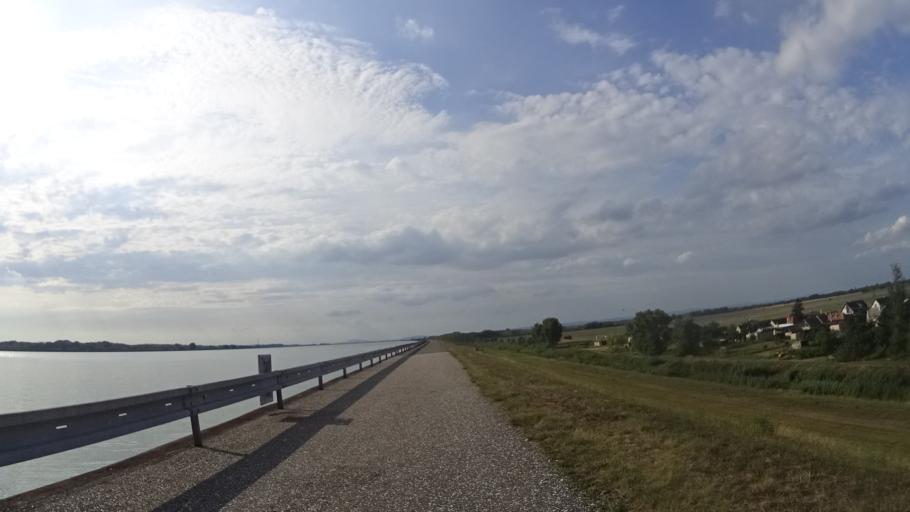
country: HU
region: Gyor-Moson-Sopron
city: Halaszi
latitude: 47.9524
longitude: 17.4360
